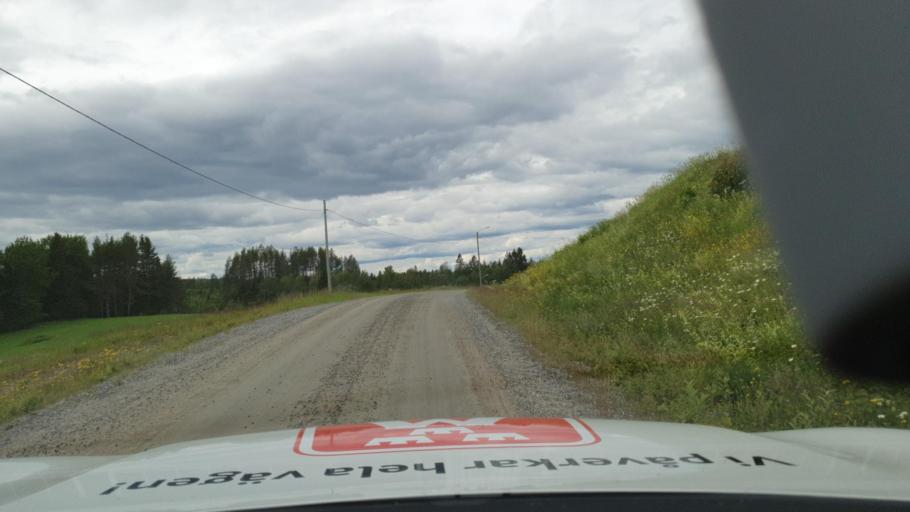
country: SE
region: Vaesterbotten
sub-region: Bjurholms Kommun
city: Bjurholm
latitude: 63.7565
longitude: 19.2690
